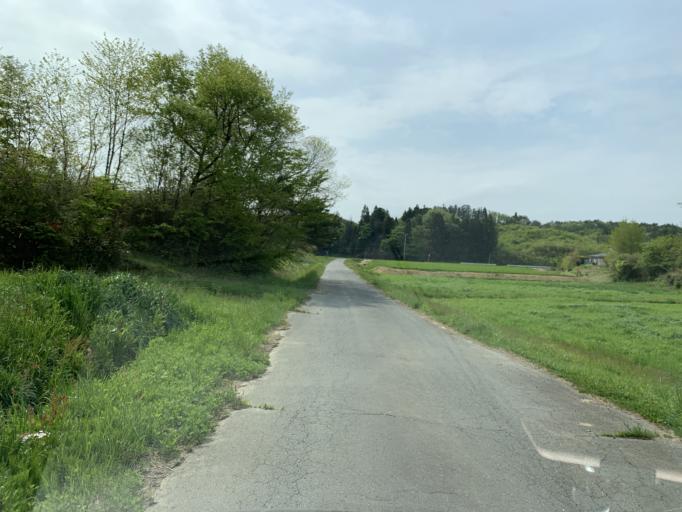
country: JP
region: Iwate
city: Ichinoseki
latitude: 38.8811
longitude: 141.0608
